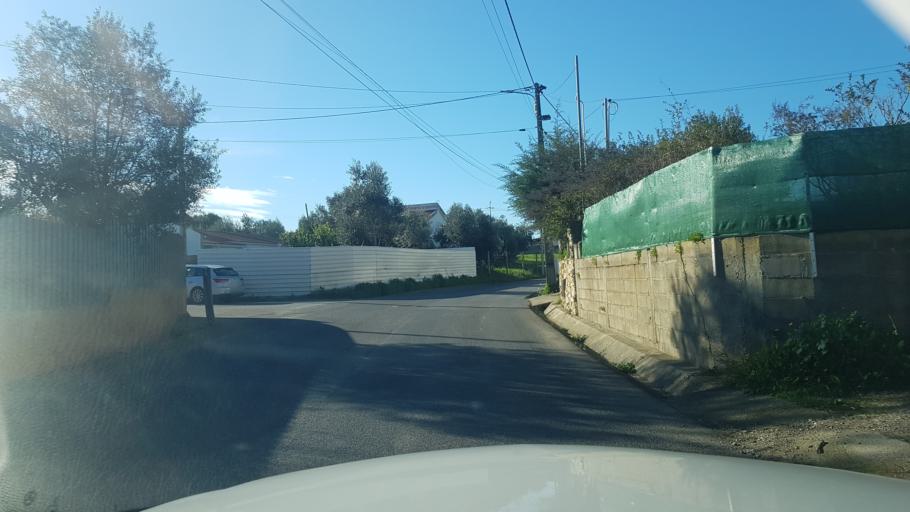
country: PT
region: Santarem
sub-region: Torres Novas
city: Riachos
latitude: 39.4774
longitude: -8.5017
